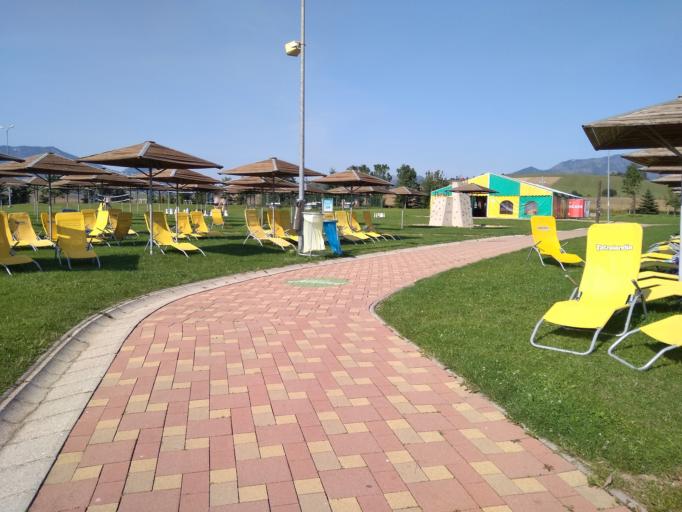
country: SK
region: Zilinsky
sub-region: Okres Liptovsky Mikulas
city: Liptovsky Mikulas
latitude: 49.1073
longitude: 19.5699
